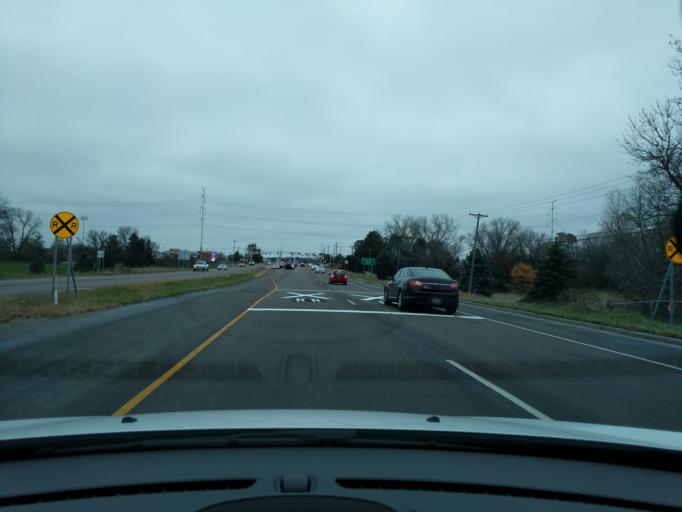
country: US
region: Minnesota
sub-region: Ramsey County
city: Roseville
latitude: 45.0184
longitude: -93.1668
